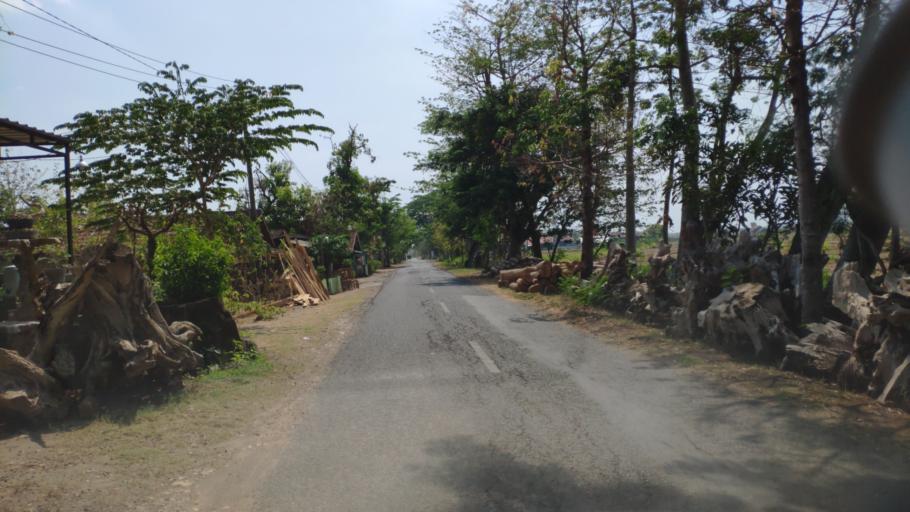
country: ID
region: Central Java
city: Bangkle
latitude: -6.9810
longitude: 111.4312
